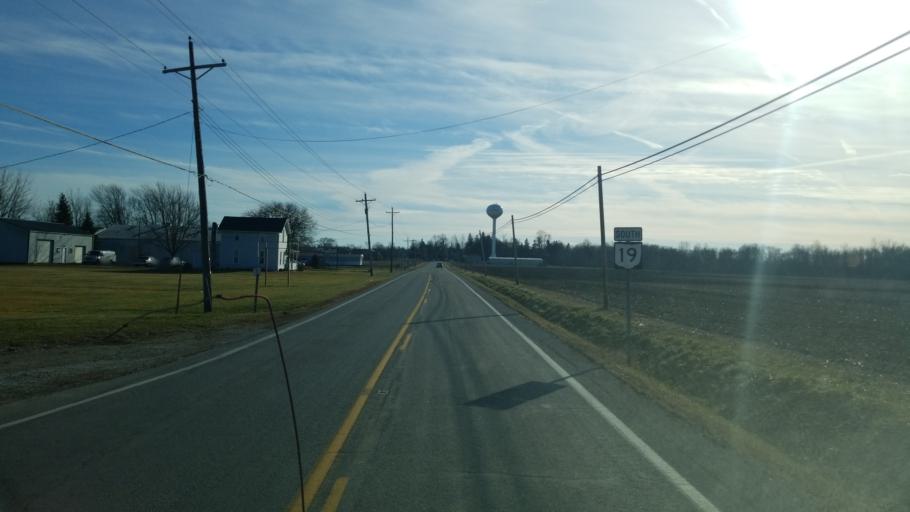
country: US
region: Ohio
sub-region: Sandusky County
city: Green Springs
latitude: 41.2712
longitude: -83.0525
